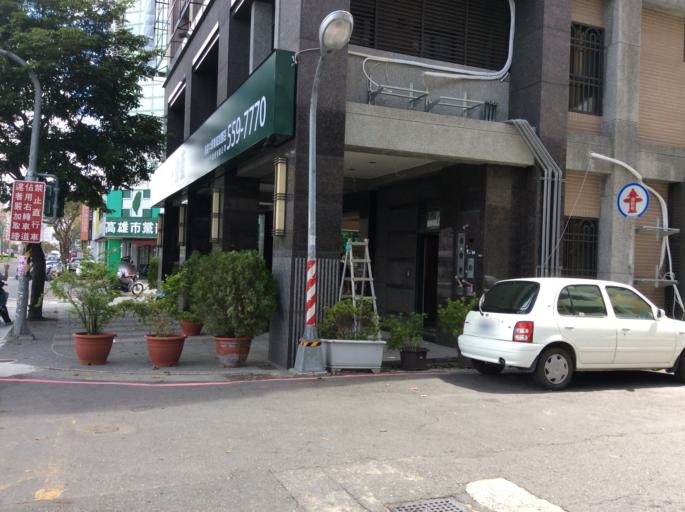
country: TW
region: Kaohsiung
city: Kaohsiung
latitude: 22.6515
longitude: 120.2919
